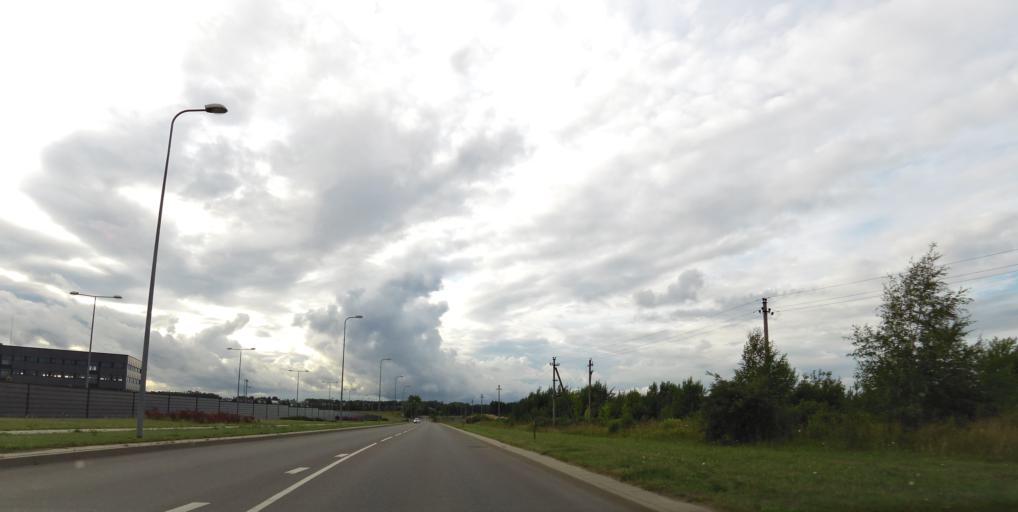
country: LT
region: Vilnius County
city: Justiniskes
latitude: 54.7064
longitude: 25.2052
